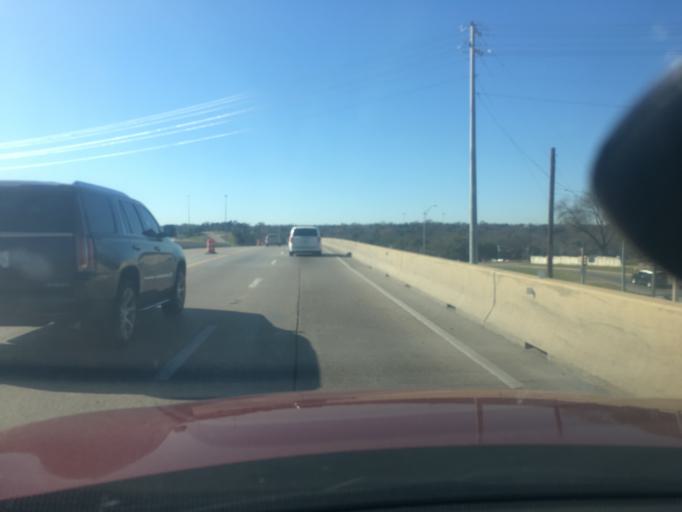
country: US
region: Texas
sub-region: Dallas County
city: Cockrell Hill
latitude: 32.6989
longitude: -96.8394
